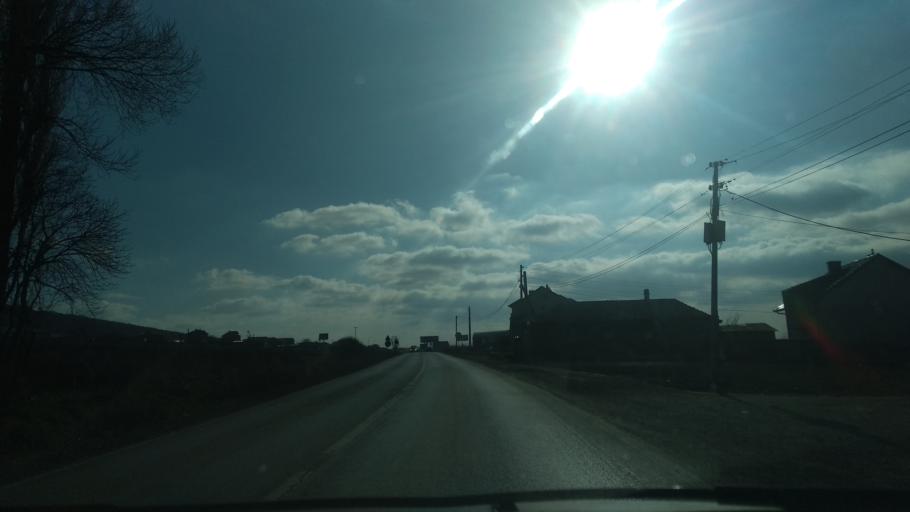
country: XK
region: Pristina
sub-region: Komuna e Prishtines
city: Pristina
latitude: 42.7369
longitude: 21.1416
